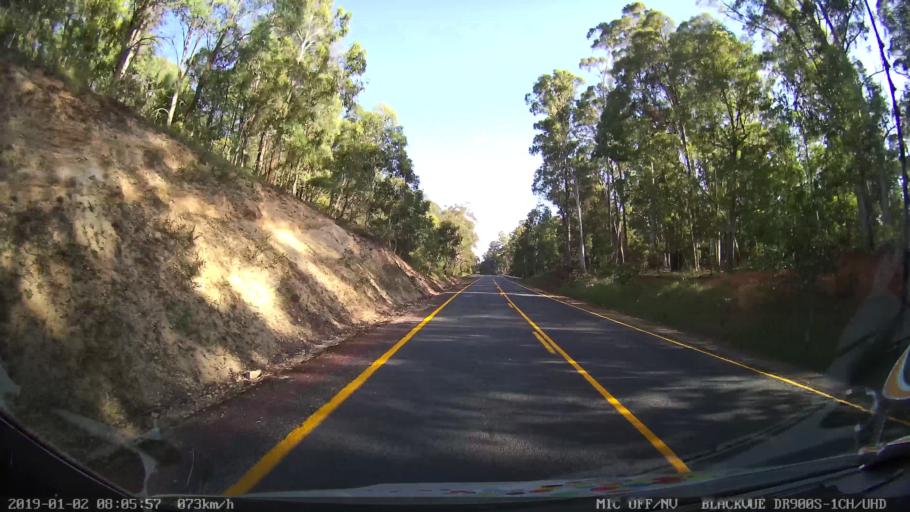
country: AU
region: New South Wales
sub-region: Tumut Shire
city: Tumut
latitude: -35.6455
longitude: 148.3872
